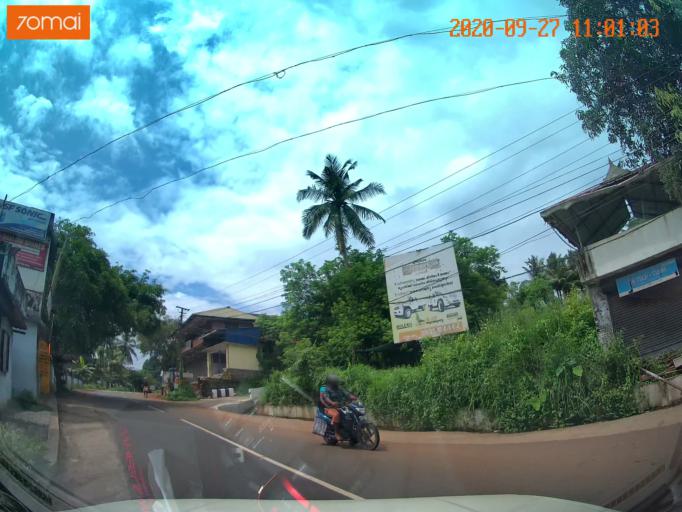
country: IN
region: Kerala
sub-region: Thrissur District
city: Irinjalakuda
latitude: 10.4216
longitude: 76.2671
